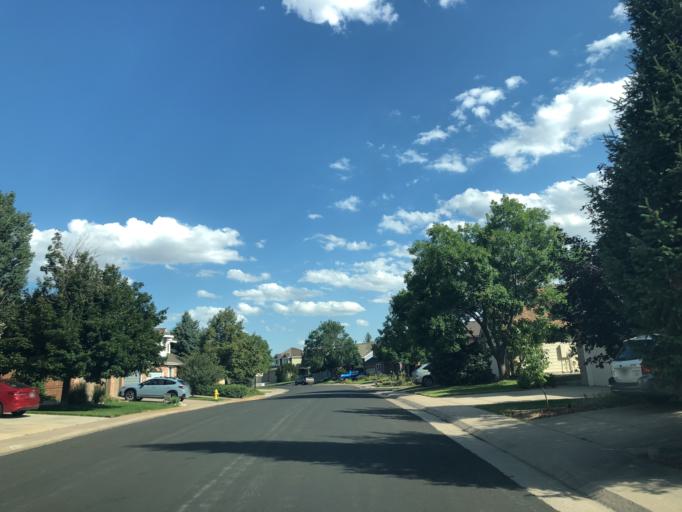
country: US
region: Colorado
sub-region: Arapahoe County
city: Dove Valley
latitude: 39.6087
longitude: -104.7661
